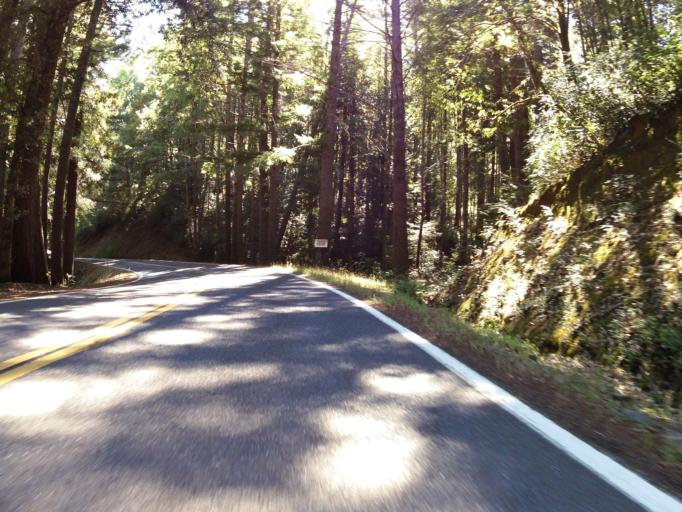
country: US
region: California
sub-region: Humboldt County
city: Redway
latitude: 39.8197
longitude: -123.7831
